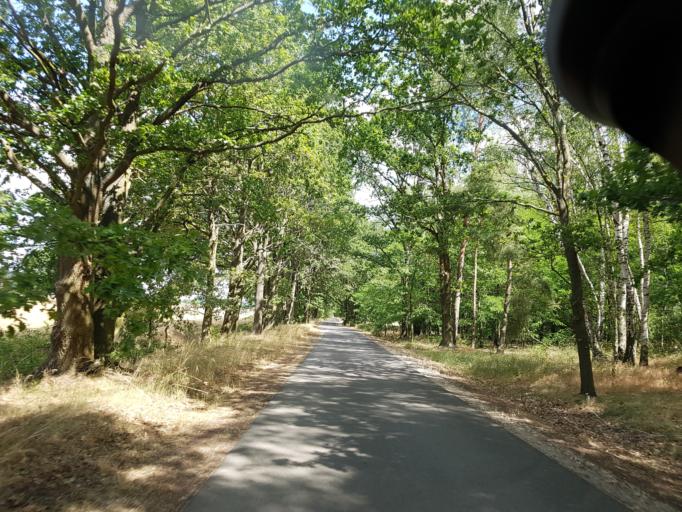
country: DE
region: Brandenburg
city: Cottbus
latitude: 51.6950
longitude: 14.3131
